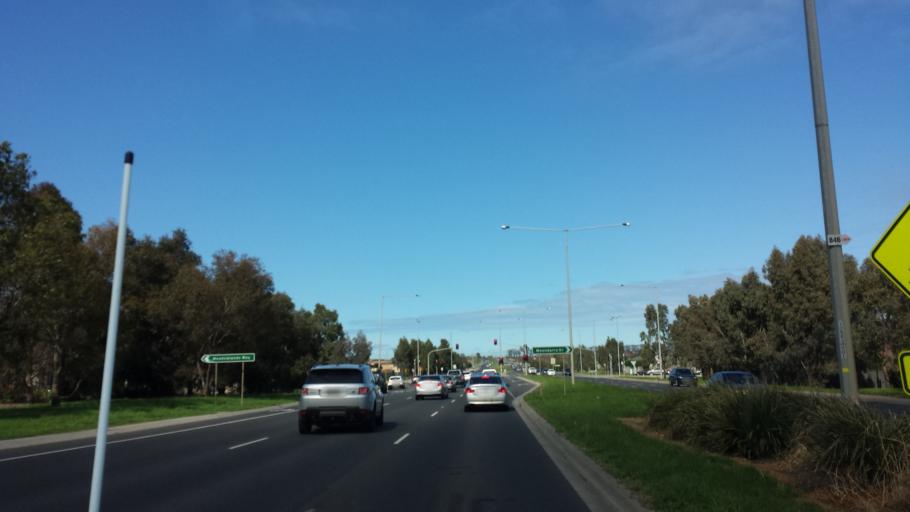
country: AU
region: Victoria
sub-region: Casey
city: Berwick
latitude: -38.0669
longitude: 145.3370
